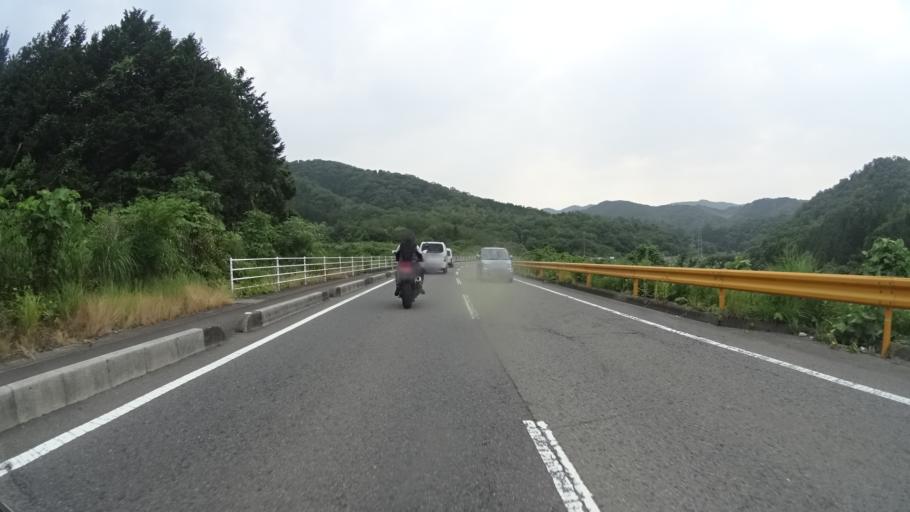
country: JP
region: Yamaguchi
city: Onoda
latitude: 34.1681
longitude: 131.1650
